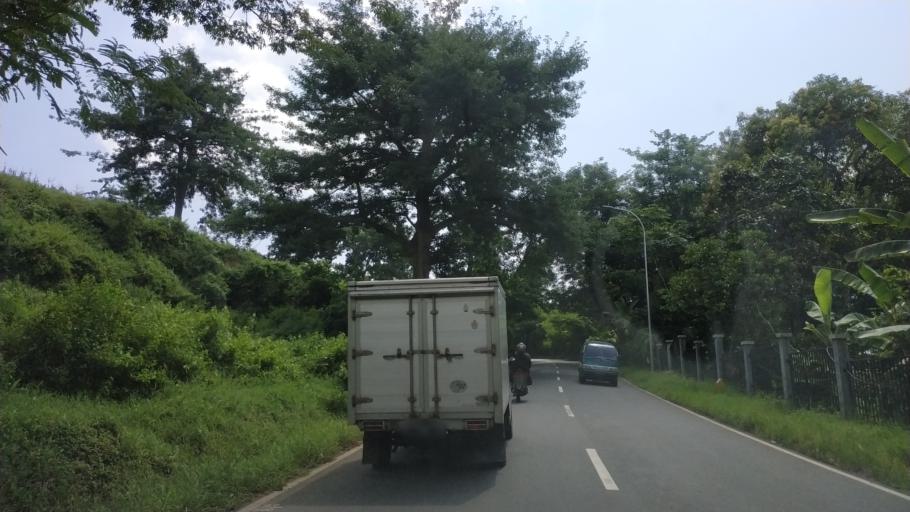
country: ID
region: Central Java
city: Weleri
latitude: -7.0019
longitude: 110.0661
